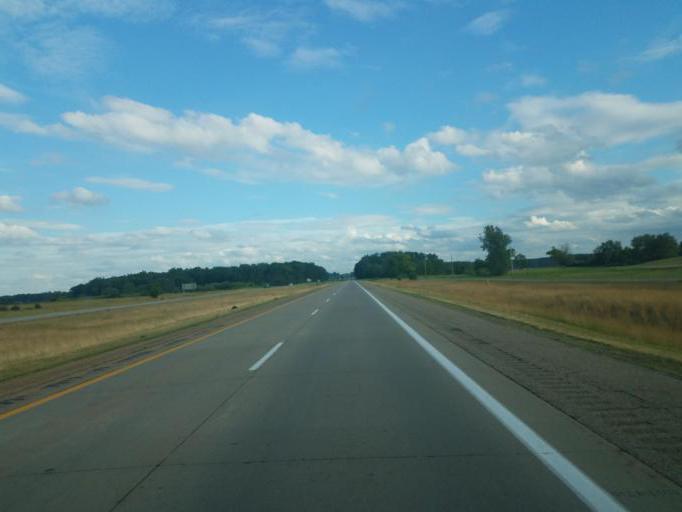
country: US
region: Indiana
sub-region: Steuben County
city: Fremont
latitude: 41.7846
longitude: -84.9919
